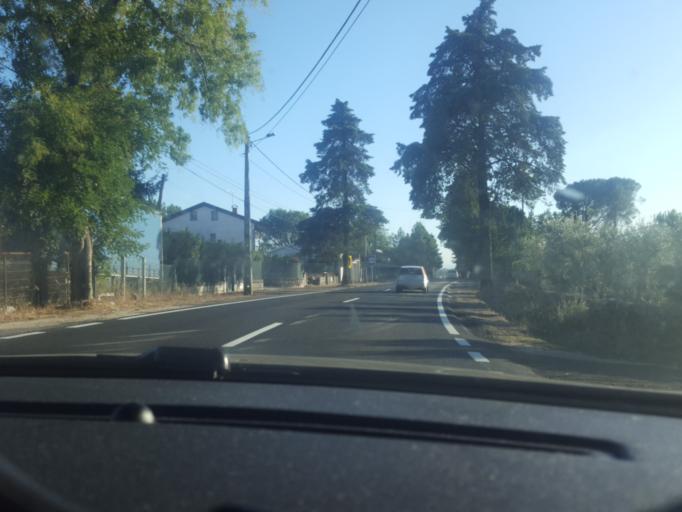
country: PT
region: Viseu
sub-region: Mangualde
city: Mangualde
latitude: 40.5808
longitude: -7.8066
